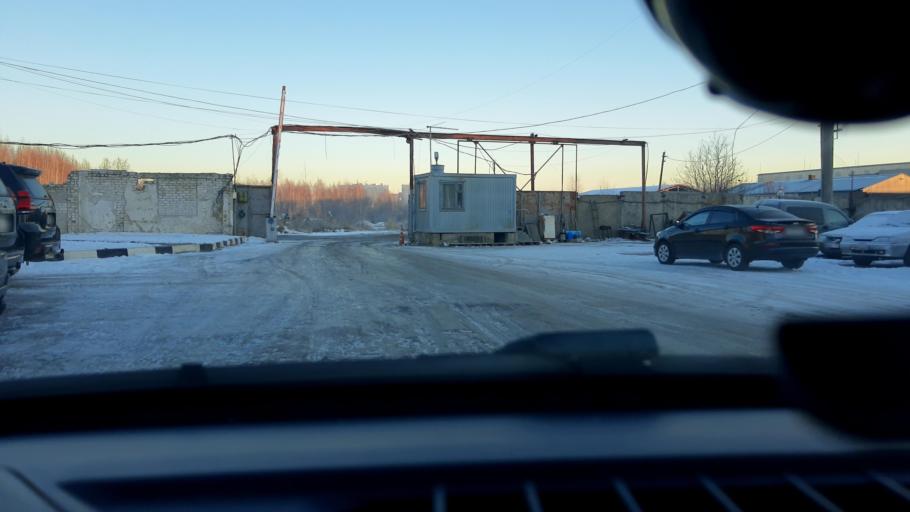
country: RU
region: Nizjnij Novgorod
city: Gorbatovka
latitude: 56.3538
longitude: 43.7910
